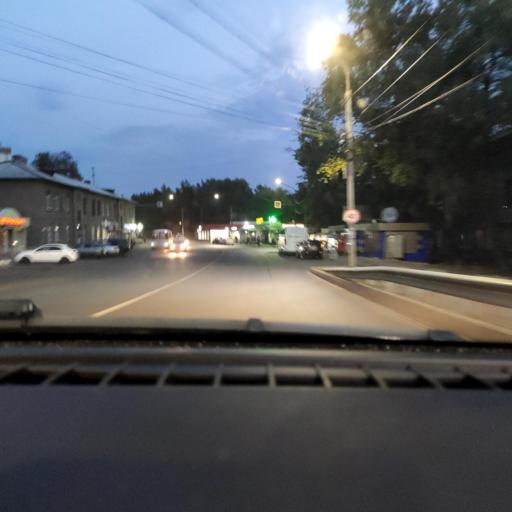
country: RU
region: Voronezj
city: Voronezh
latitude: 51.7245
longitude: 39.2628
